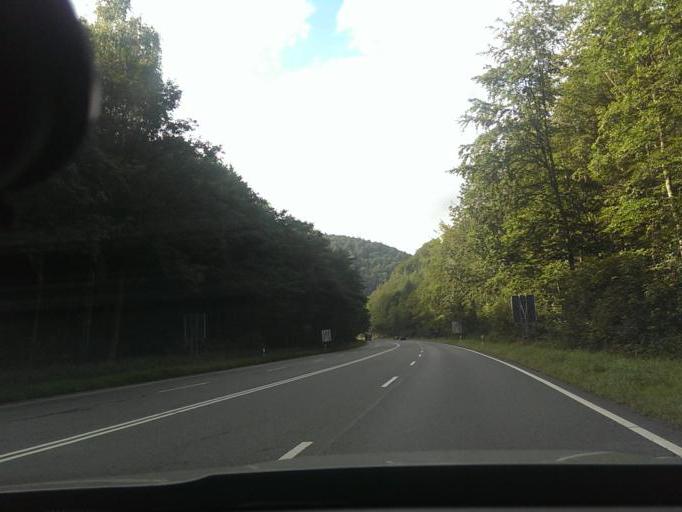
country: DE
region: Lower Saxony
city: Bad Harzburg
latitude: 51.8636
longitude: 10.5559
